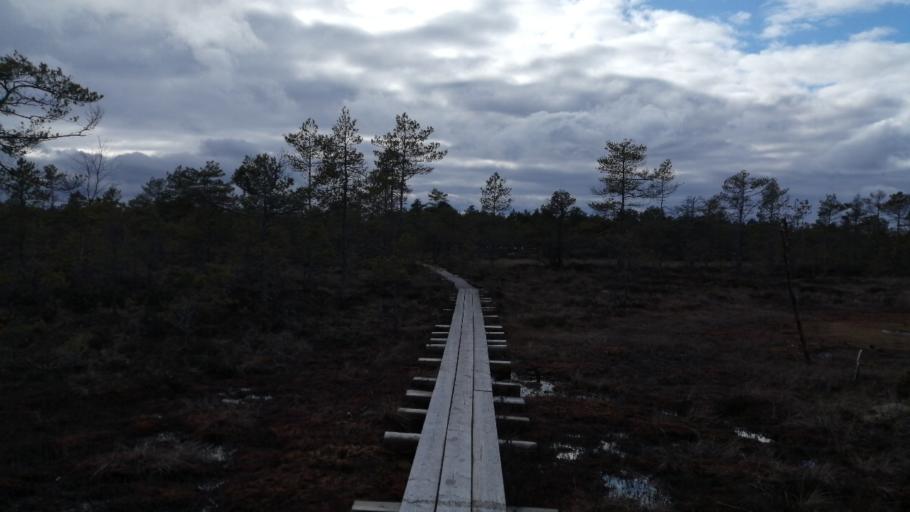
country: EE
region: Ida-Virumaa
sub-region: Kohtla-Nomme vald
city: Kohtla-Nomme
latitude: 59.1707
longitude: 27.2706
